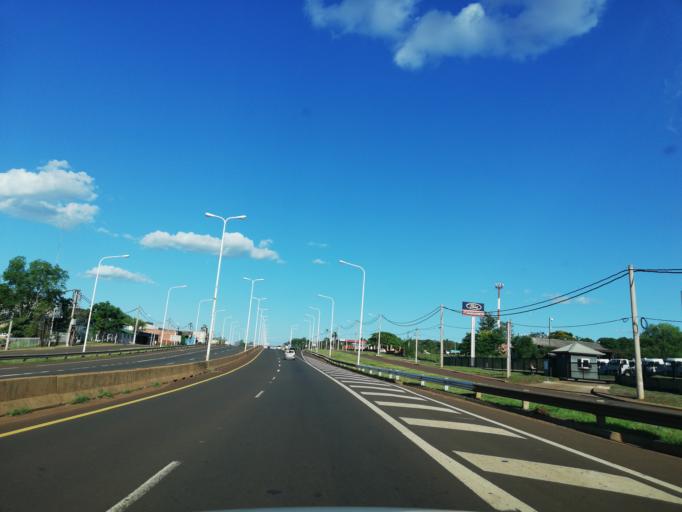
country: AR
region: Misiones
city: Garupa
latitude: -27.4615
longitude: -55.8433
